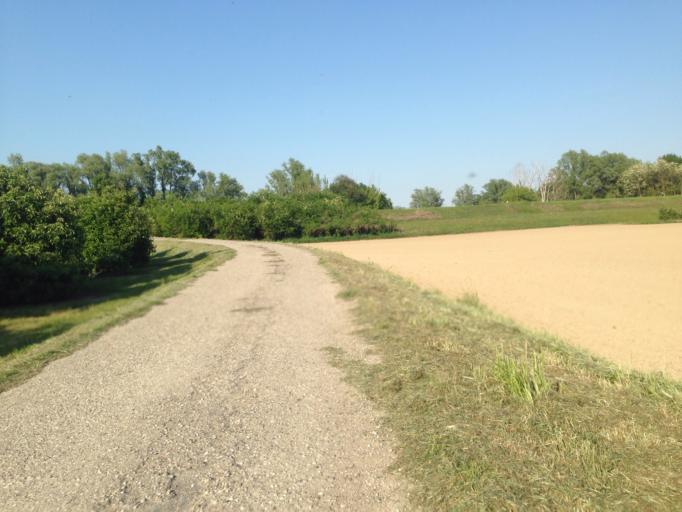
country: IT
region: Veneto
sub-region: Provincia di Verona
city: Zevio
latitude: 45.3715
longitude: 11.1513
